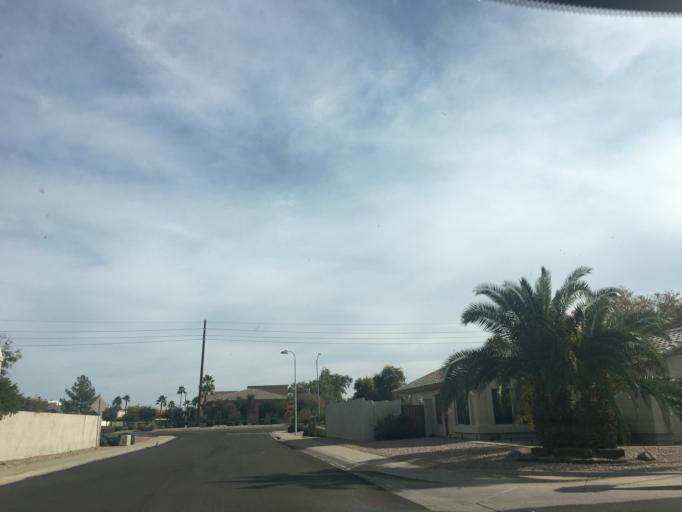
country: US
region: Arizona
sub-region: Maricopa County
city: Gilbert
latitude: 33.3488
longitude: -111.8078
